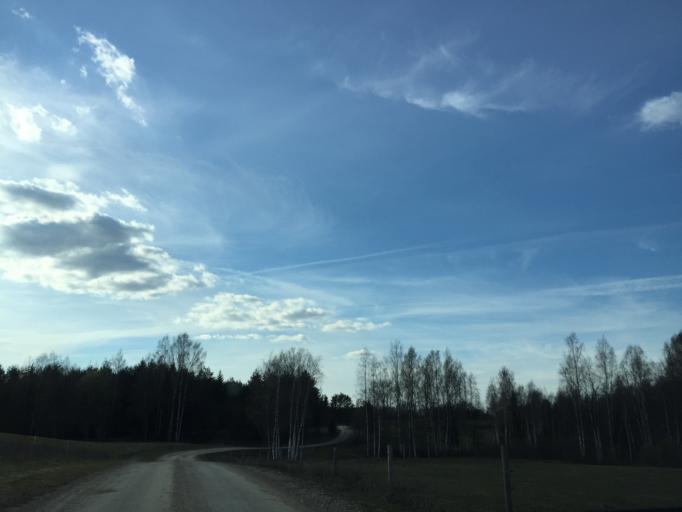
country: EE
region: Tartu
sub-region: Noo vald
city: Noo
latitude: 58.1328
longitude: 26.5873
